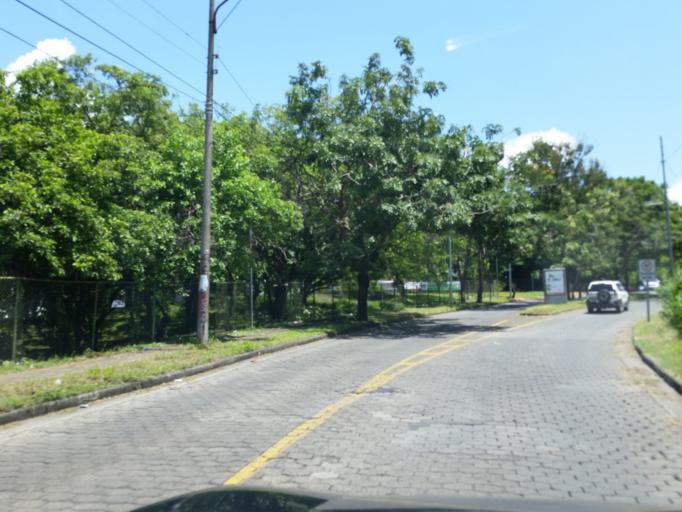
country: NI
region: Managua
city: Managua
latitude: 12.1040
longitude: -86.2705
